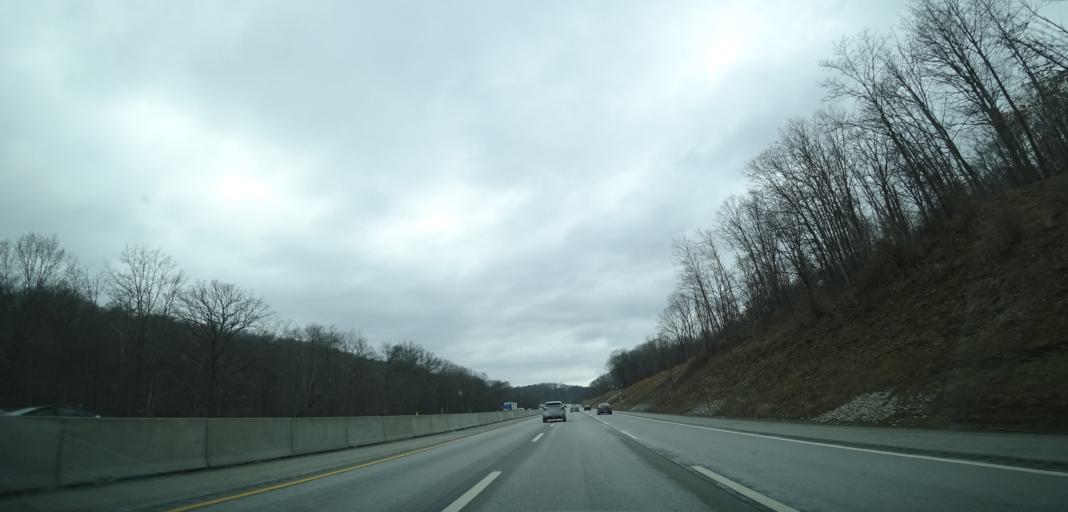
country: US
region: Pennsylvania
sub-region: Allegheny County
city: Gibsonia
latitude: 40.6347
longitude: -79.9895
